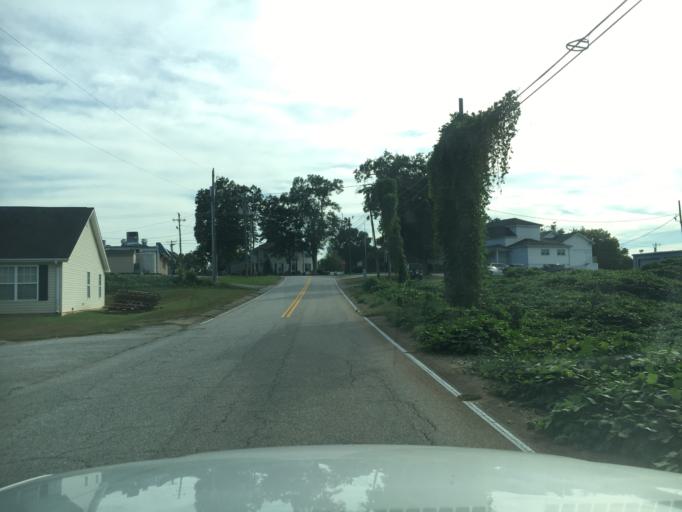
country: US
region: South Carolina
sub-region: Spartanburg County
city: Duncan
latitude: 34.9385
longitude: -82.1387
